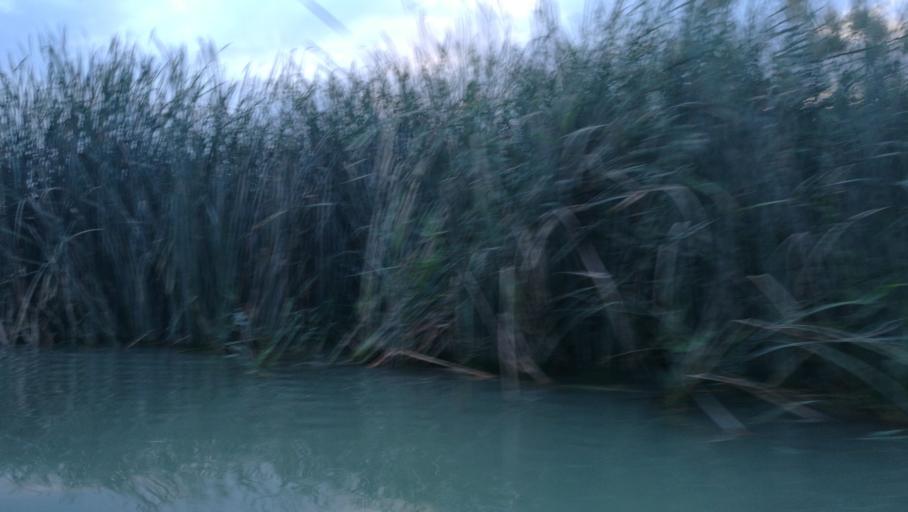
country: IQ
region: Dhi Qar
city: Al Jabayish
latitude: 30.9816
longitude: 47.0369
